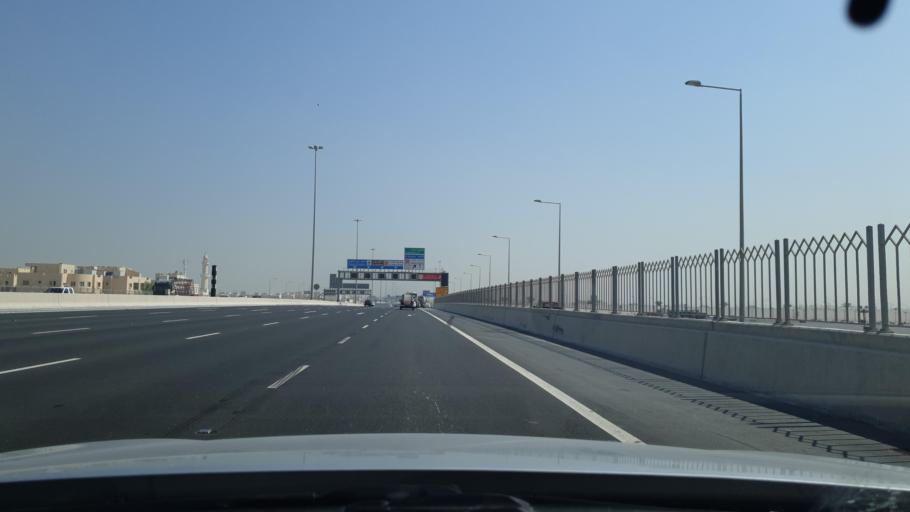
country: QA
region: Baladiyat ad Dawhah
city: Doha
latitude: 25.2254
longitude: 51.5501
